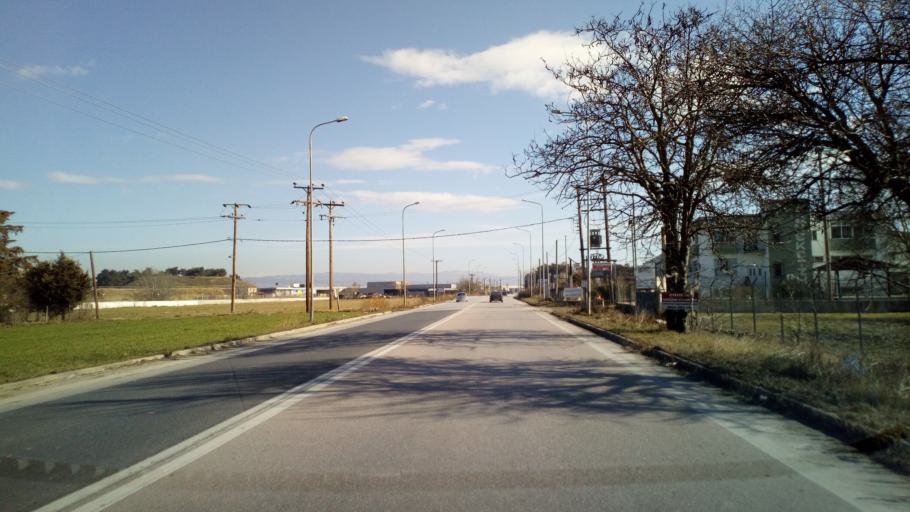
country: GR
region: Central Macedonia
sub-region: Nomos Thessalonikis
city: Lagyna
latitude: 40.7336
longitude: 23.0275
